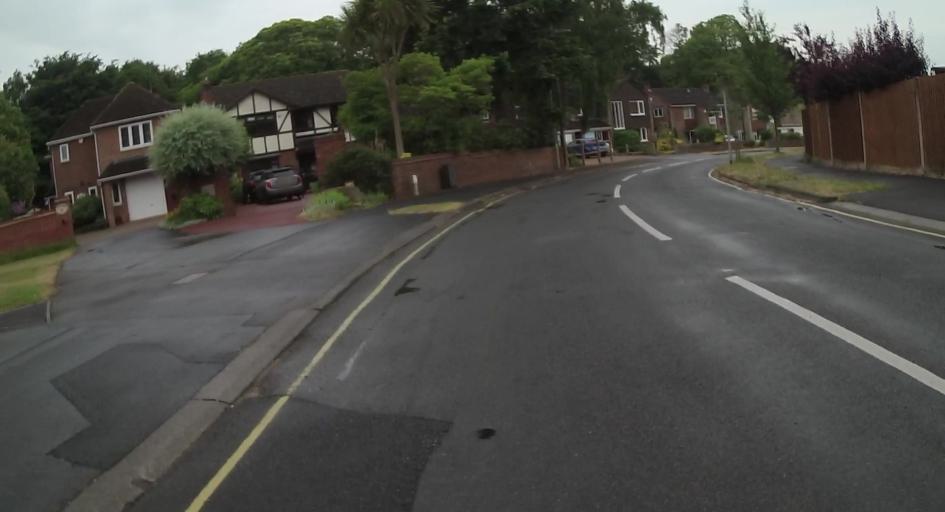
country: GB
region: England
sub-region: Hampshire
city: Farnborough
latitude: 51.2995
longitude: -0.7573
